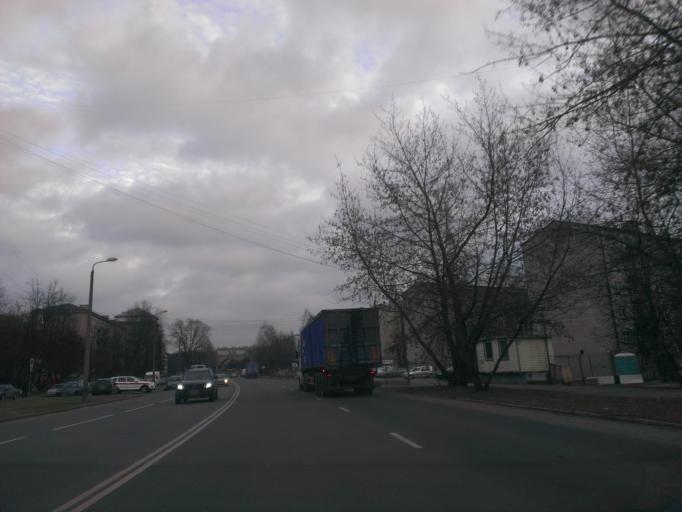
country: LV
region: Riga
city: Riga
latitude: 56.9725
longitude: 24.1302
